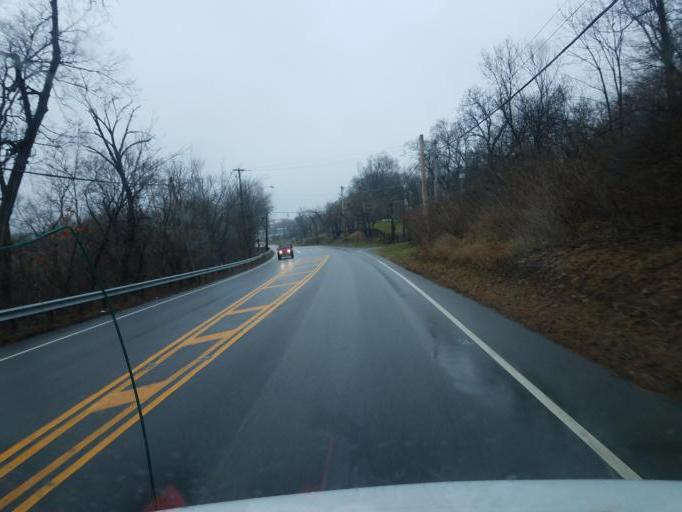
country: US
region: Ohio
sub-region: Franklin County
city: Dublin
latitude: 40.0949
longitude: -83.1082
